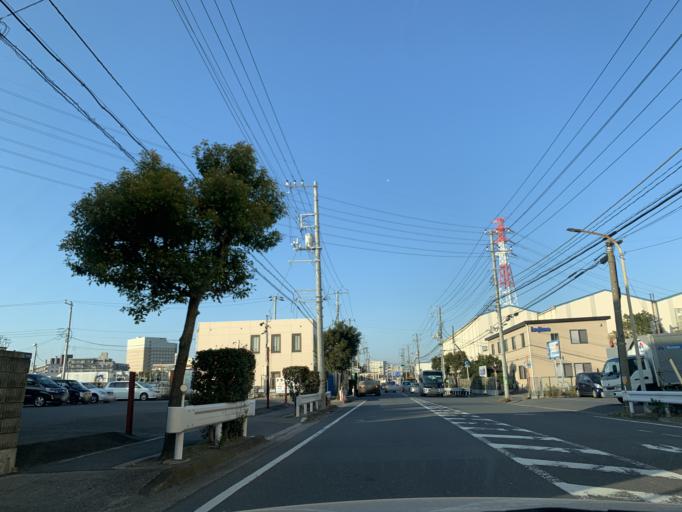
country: JP
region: Chiba
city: Funabashi
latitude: 35.6983
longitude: 139.9548
